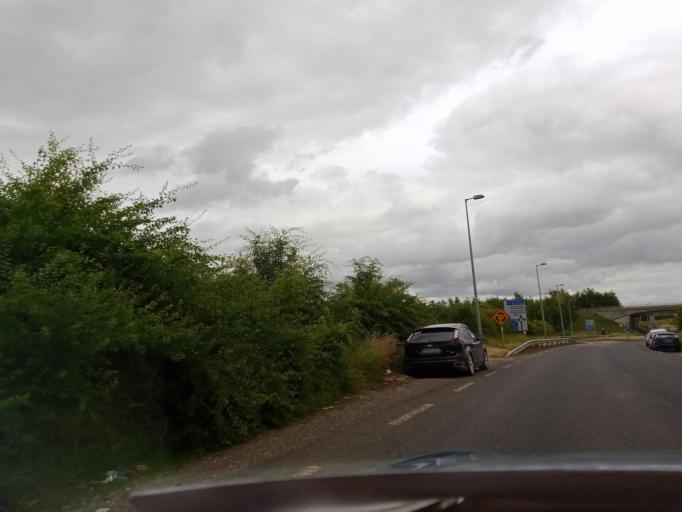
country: IE
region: Leinster
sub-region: Kilkenny
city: Thomastown
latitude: 52.4856
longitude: -7.2436
